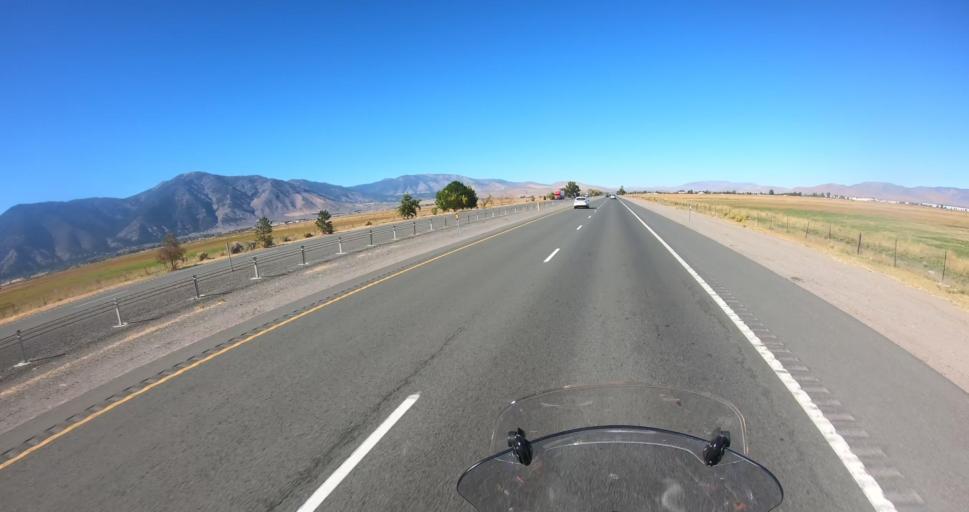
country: US
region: Nevada
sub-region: Douglas County
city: Minden
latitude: 38.9808
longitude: -119.7786
